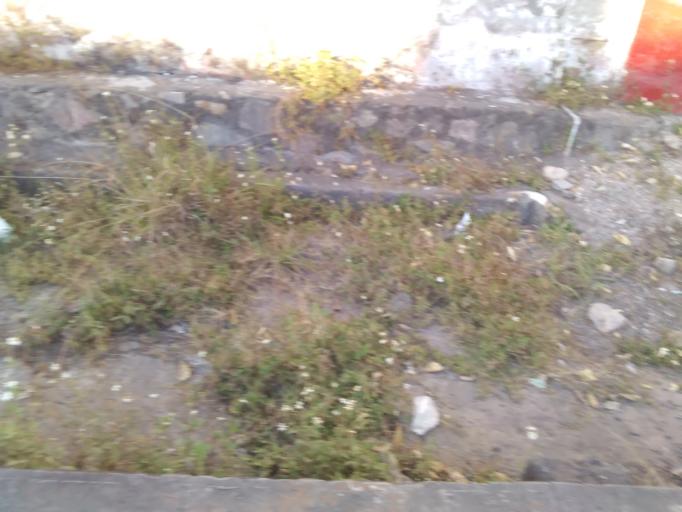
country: MX
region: Nayarit
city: Tepic
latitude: 21.5046
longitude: -104.8825
